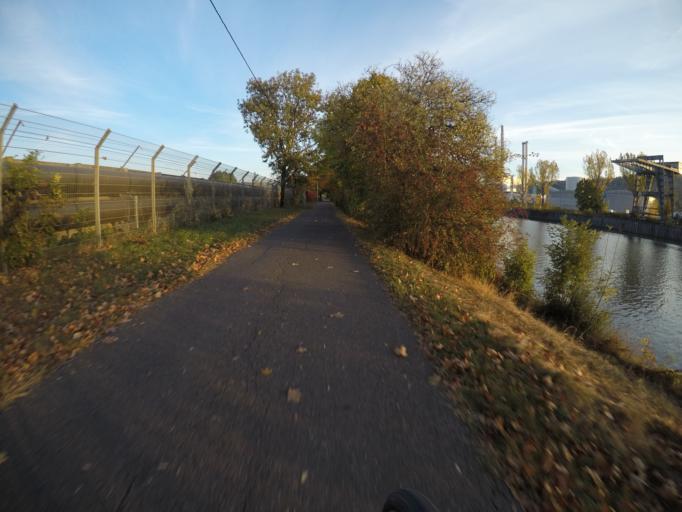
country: DE
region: Baden-Wuerttemberg
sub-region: Regierungsbezirk Stuttgart
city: Stuttgart-Ost
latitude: 48.7875
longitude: 9.2281
